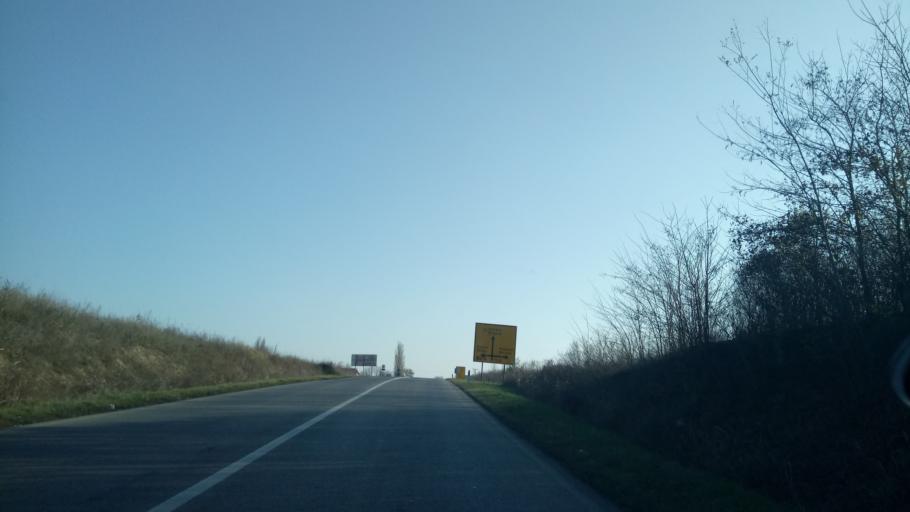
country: RS
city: Cortanovci
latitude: 45.1121
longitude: 20.0248
